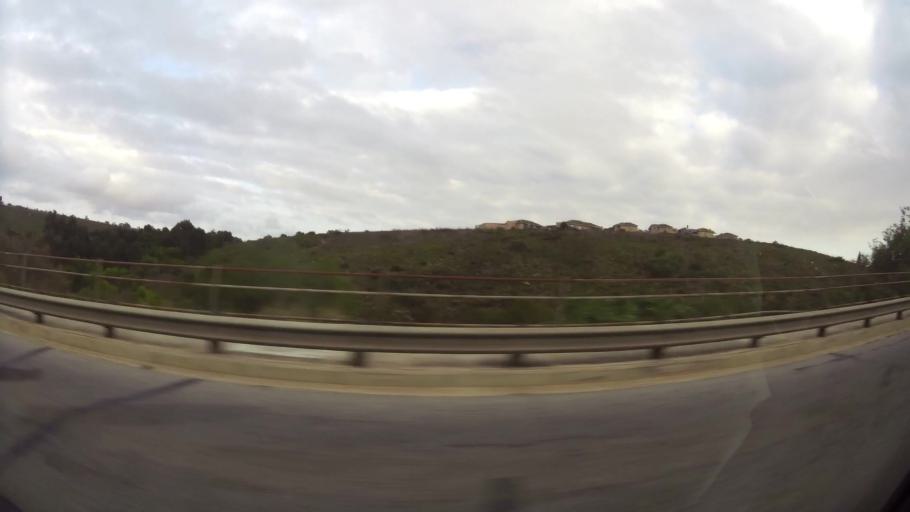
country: ZA
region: Eastern Cape
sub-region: Nelson Mandela Bay Metropolitan Municipality
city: Port Elizabeth
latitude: -33.9522
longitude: 25.5542
